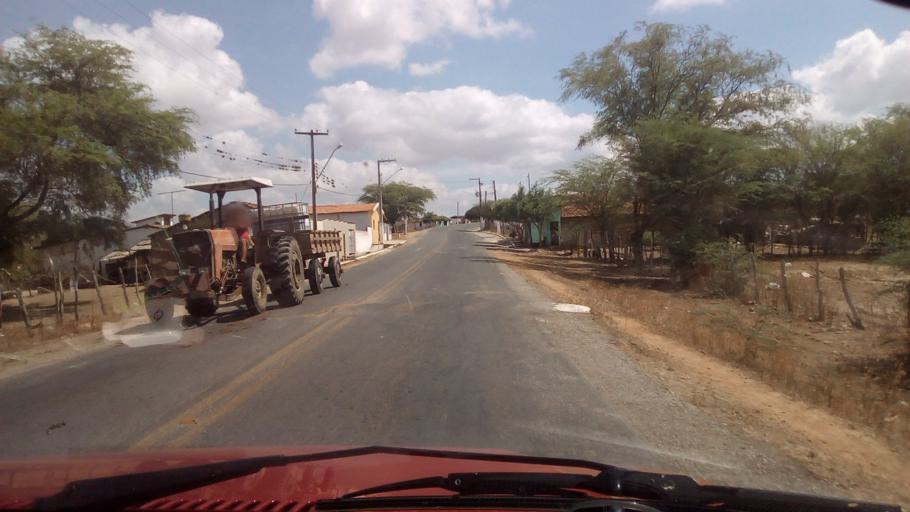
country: BR
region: Paraiba
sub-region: Dona Ines
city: Dona Ines
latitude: -6.5389
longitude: -35.6577
